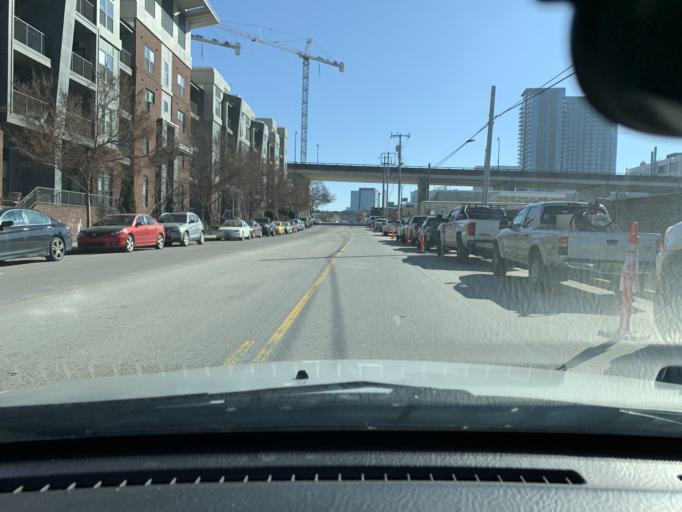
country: US
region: Tennessee
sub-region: Davidson County
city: Nashville
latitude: 36.1605
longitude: -86.7893
